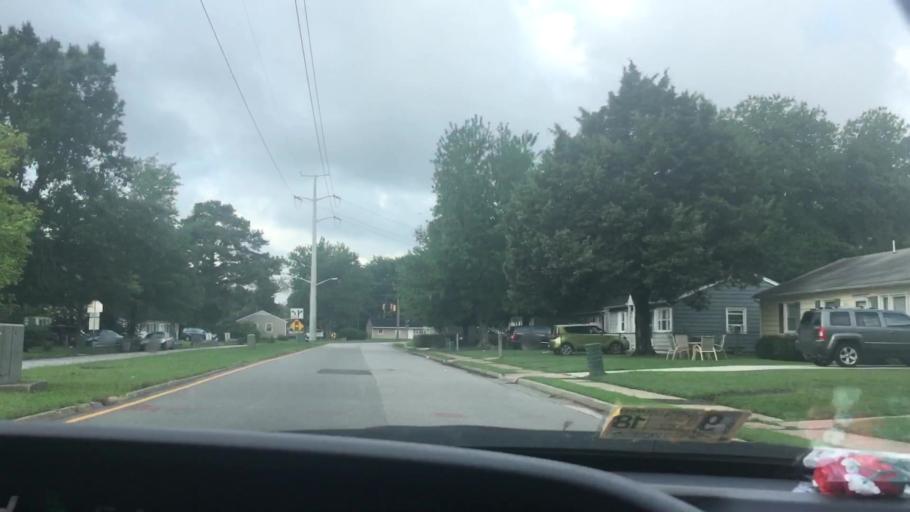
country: US
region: Virginia
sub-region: City of Hampton
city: East Hampton
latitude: 37.0442
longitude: -76.3136
